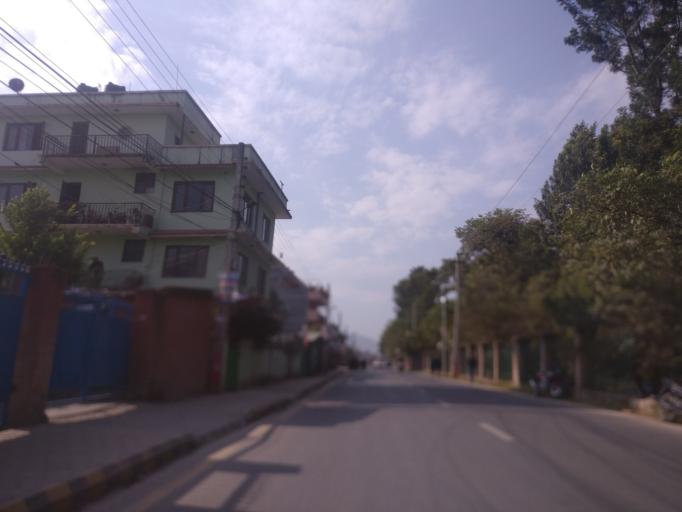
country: NP
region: Central Region
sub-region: Bagmati Zone
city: Patan
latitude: 27.6854
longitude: 85.3246
